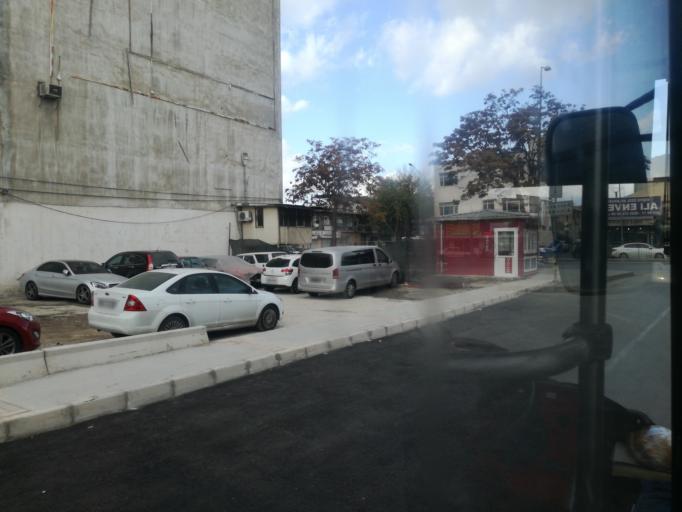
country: TR
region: Izmir
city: Izmir
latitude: 38.4227
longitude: 27.1583
